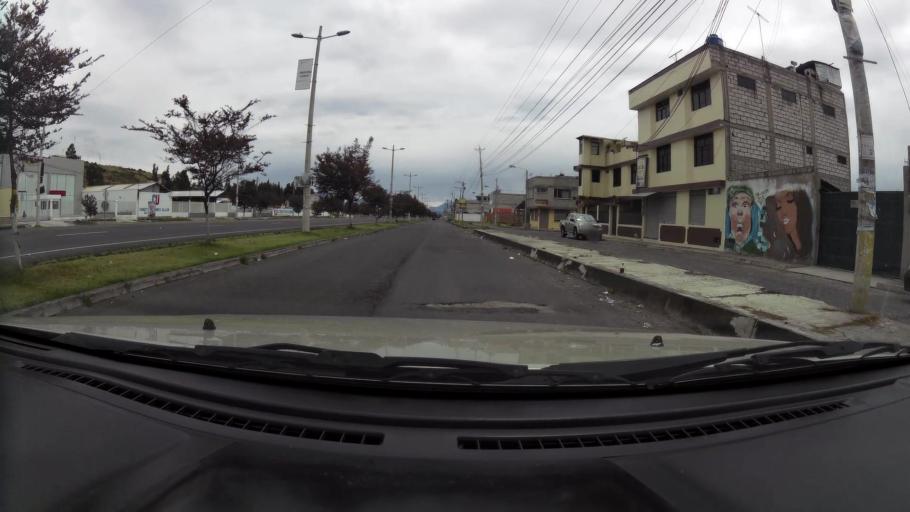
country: EC
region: Cotopaxi
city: Latacunga
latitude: -0.9602
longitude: -78.6116
